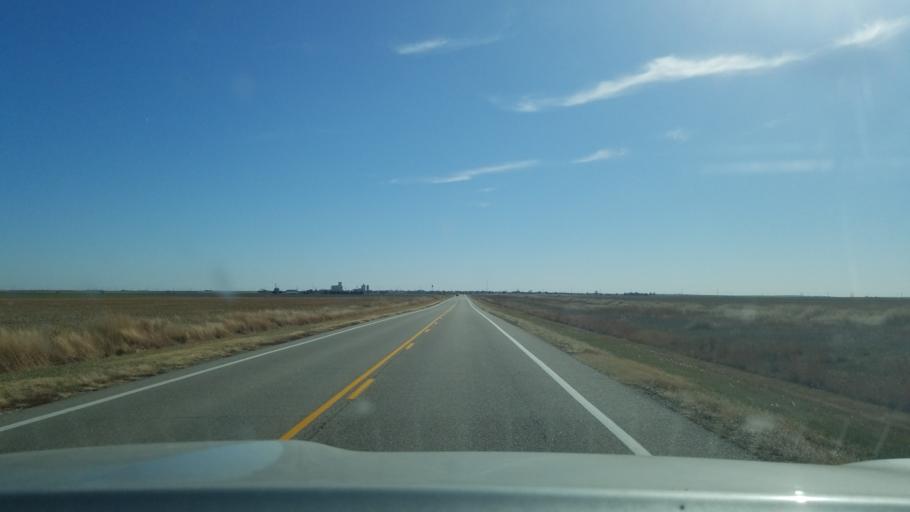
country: US
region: Kansas
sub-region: Kiowa County
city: Greensburg
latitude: 37.5697
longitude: -99.6622
